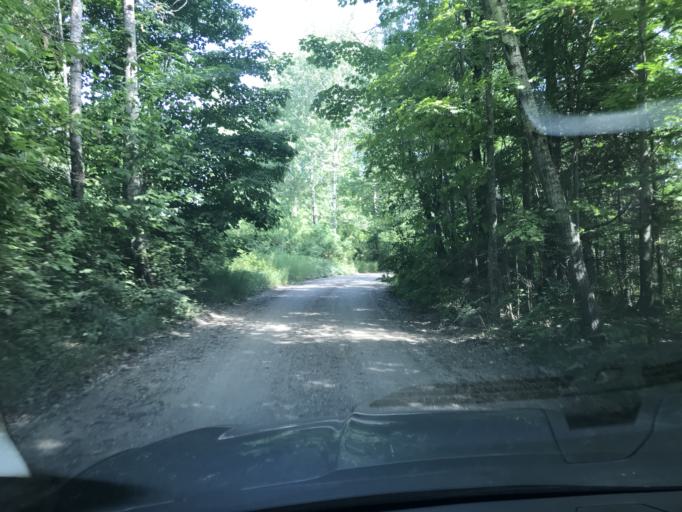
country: US
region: Michigan
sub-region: Cheboygan County
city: Cheboygan
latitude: 45.6228
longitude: -84.6776
